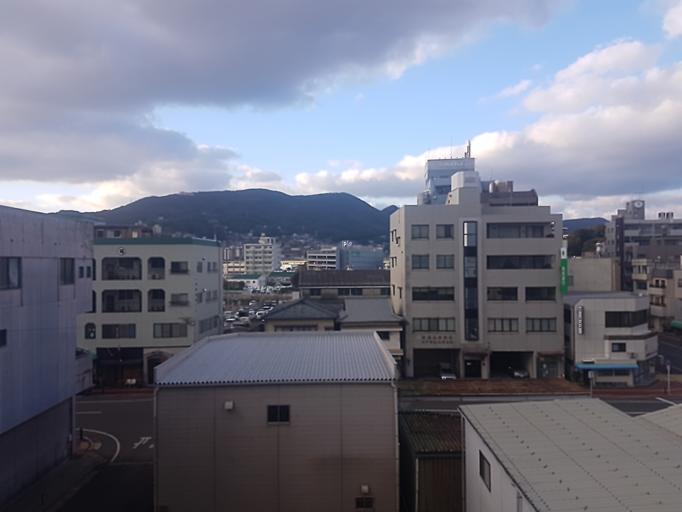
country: JP
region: Nagasaki
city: Sasebo
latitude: 33.1652
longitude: 129.7211
